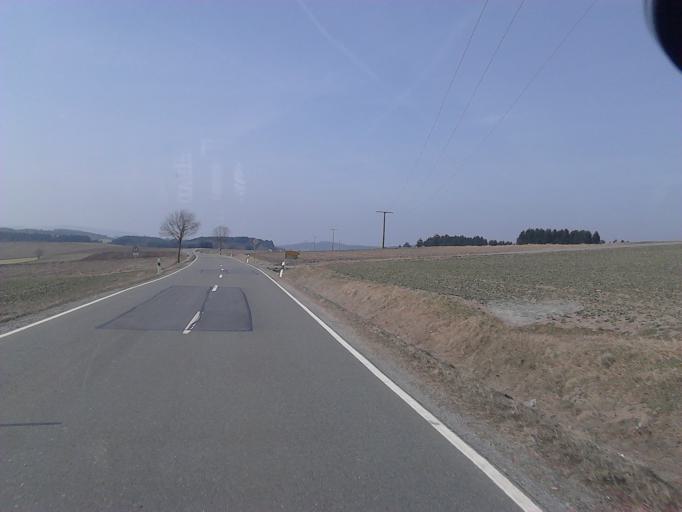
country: DE
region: Bavaria
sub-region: Upper Franconia
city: Geroldsgrun
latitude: 50.2936
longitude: 11.6202
